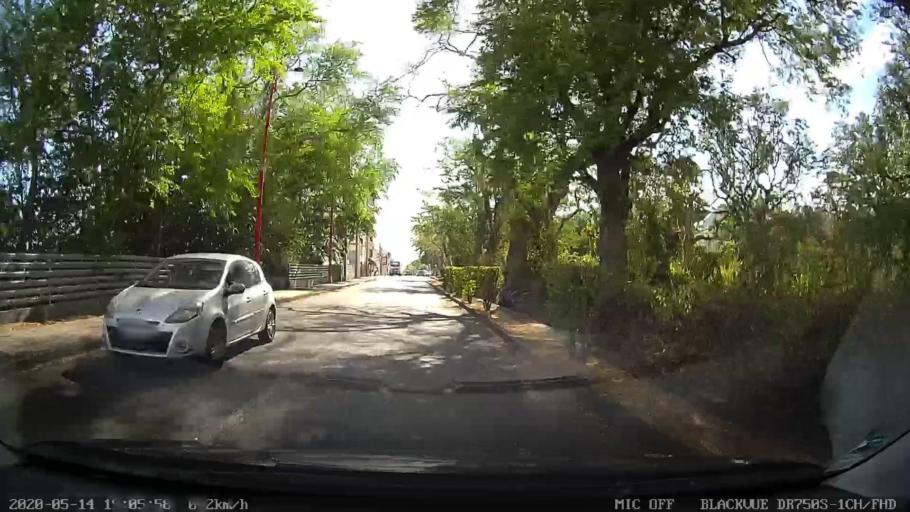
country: RE
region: Reunion
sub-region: Reunion
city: La Possession
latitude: -20.9340
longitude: 55.3344
